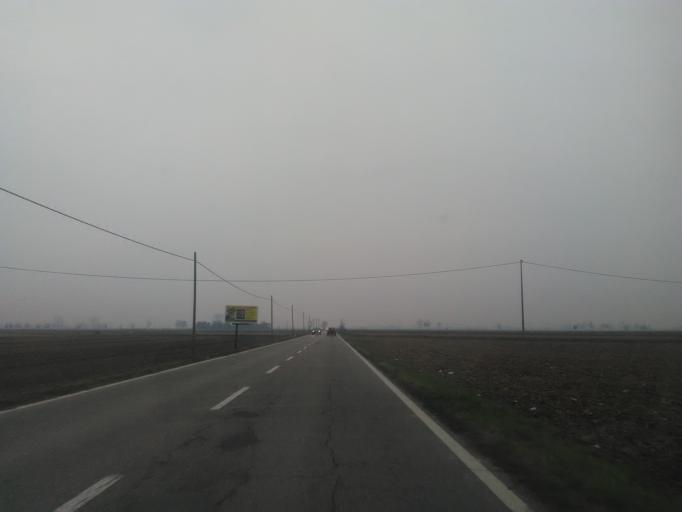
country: IT
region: Piedmont
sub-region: Provincia di Vercelli
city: Tronzano Vercellese
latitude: 45.3399
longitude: 8.1569
